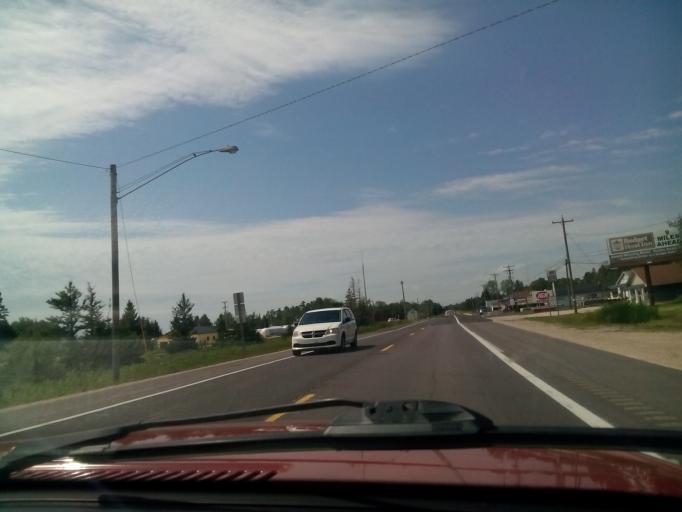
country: US
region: Michigan
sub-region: Schoolcraft County
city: Manistique
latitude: 45.9925
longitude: -86.0149
